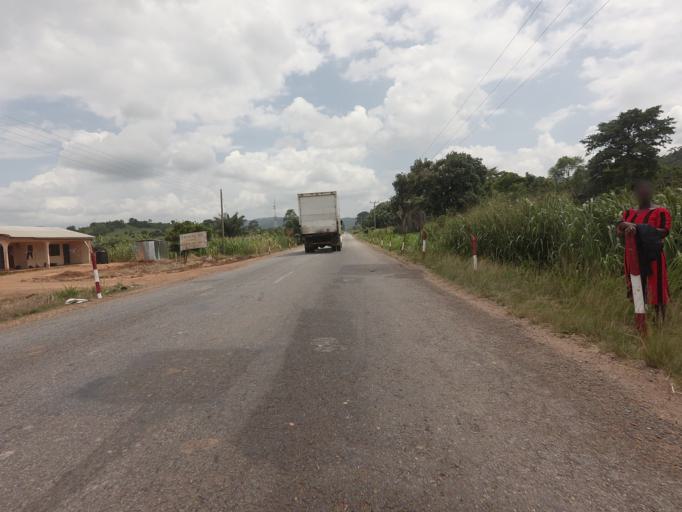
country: GH
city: Akropong
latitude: 6.3099
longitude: 0.1508
